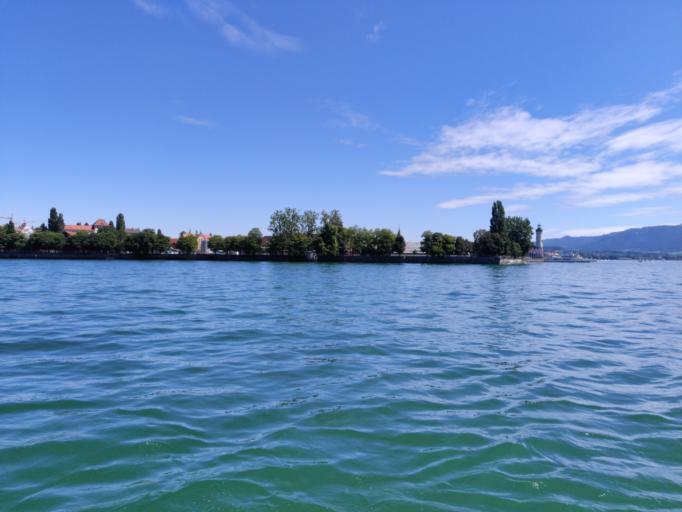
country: DE
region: Bavaria
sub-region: Swabia
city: Lindau
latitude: 47.5409
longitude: 9.6775
